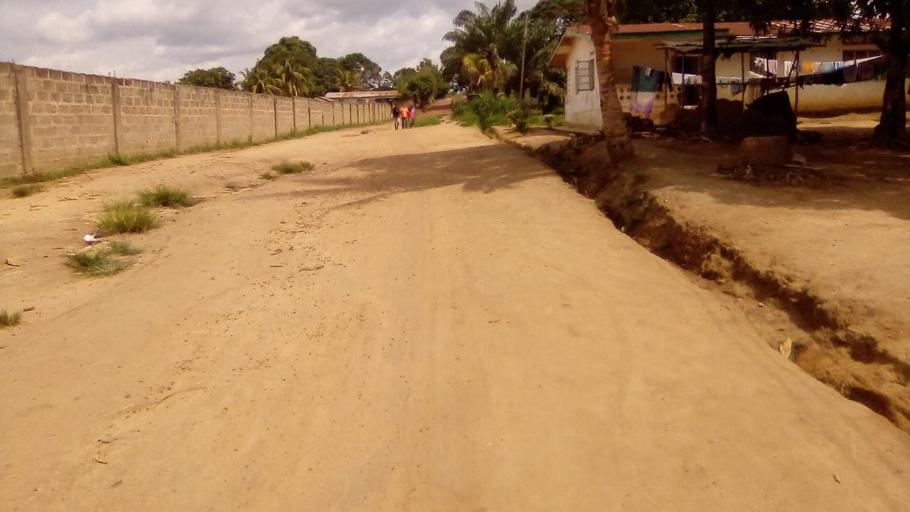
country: SL
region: Southern Province
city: Bo
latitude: 7.9650
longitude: -11.7208
